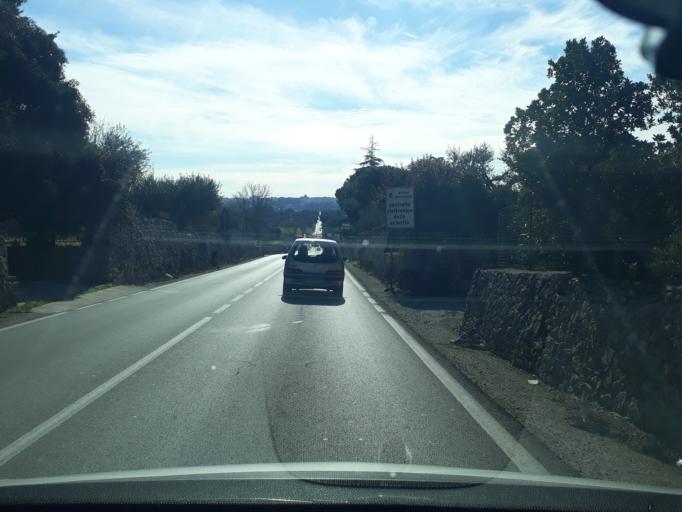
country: IT
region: Apulia
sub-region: Provincia di Bari
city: Locorotondo
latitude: 40.7407
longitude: 17.3325
